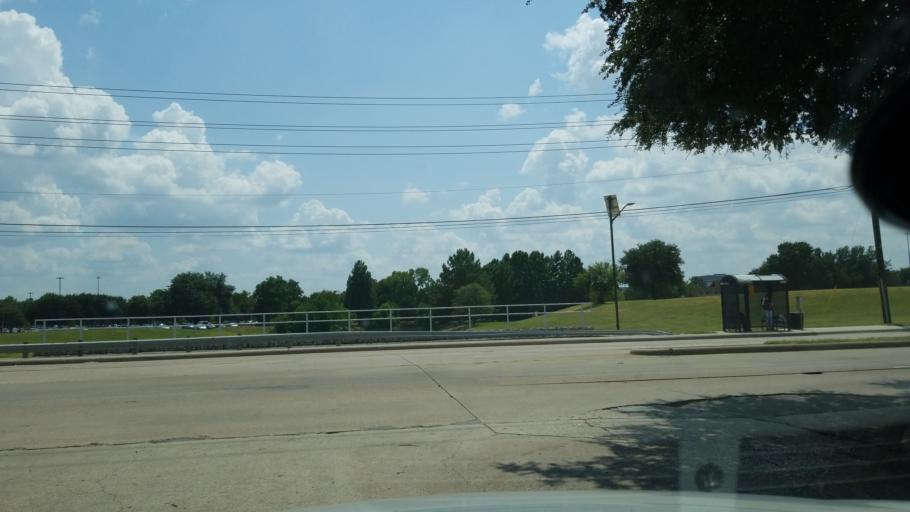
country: US
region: Texas
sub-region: Dallas County
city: Richardson
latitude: 32.9256
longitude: -96.7295
